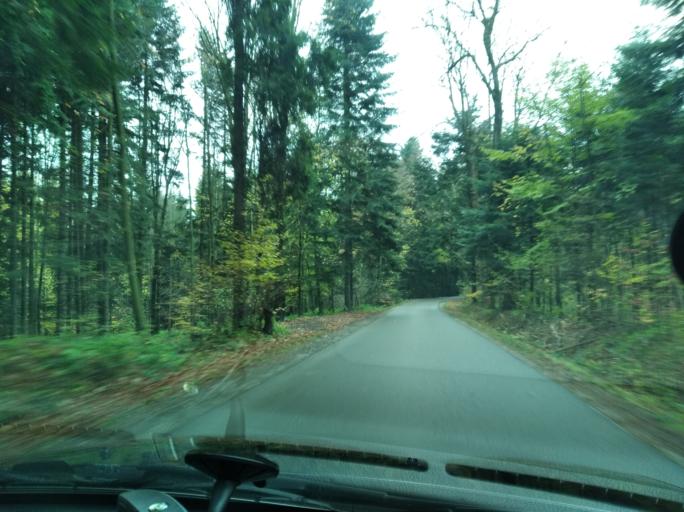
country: PL
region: Subcarpathian Voivodeship
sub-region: Powiat strzyzowski
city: Strzyzow
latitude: 49.9013
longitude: 21.7847
